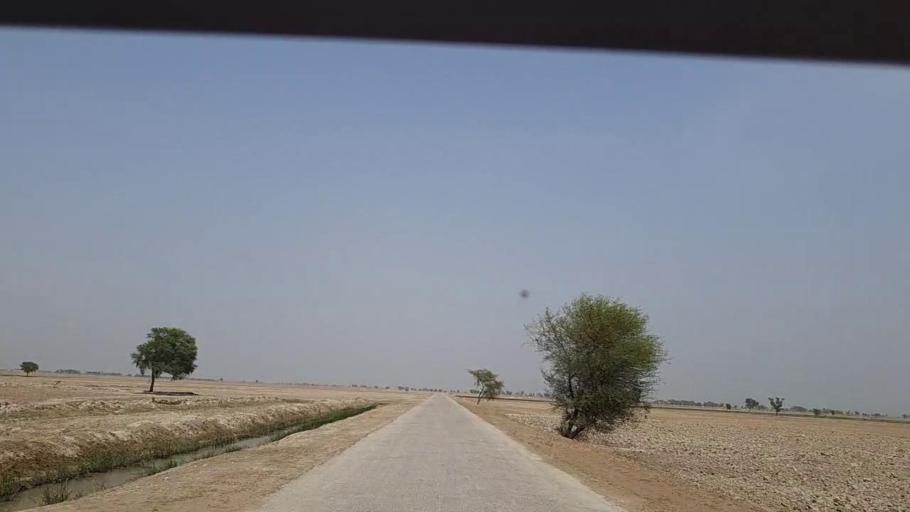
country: PK
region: Sindh
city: Khairpur Nathan Shah
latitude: 27.0303
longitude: 67.6075
